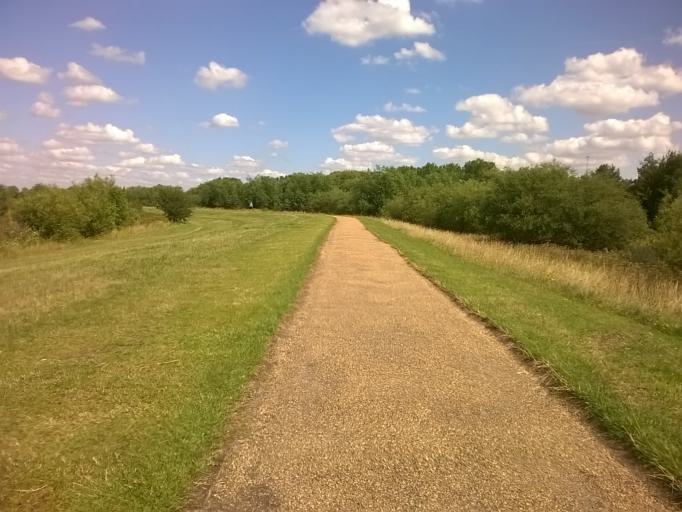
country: GB
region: England
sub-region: Milton Keynes
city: Broughton
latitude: 52.0556
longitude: -0.7145
